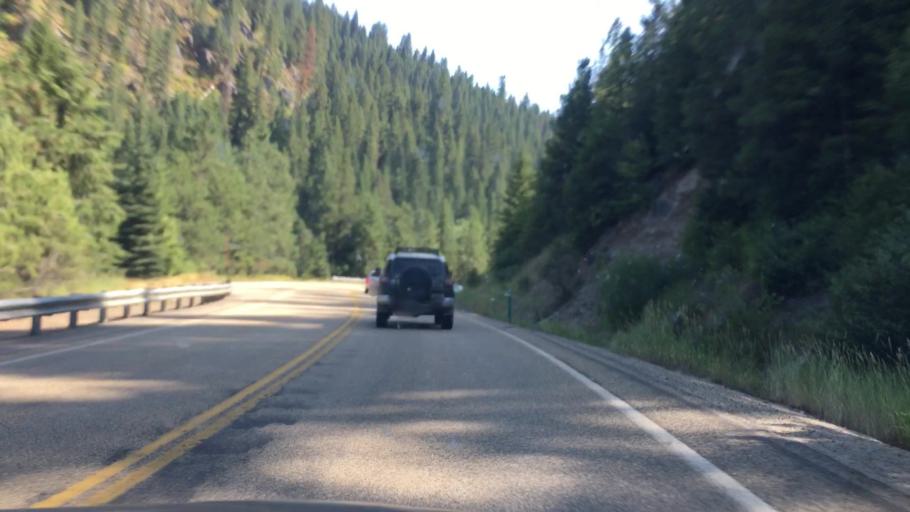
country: US
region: Idaho
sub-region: Valley County
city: Cascade
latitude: 44.2052
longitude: -116.1097
